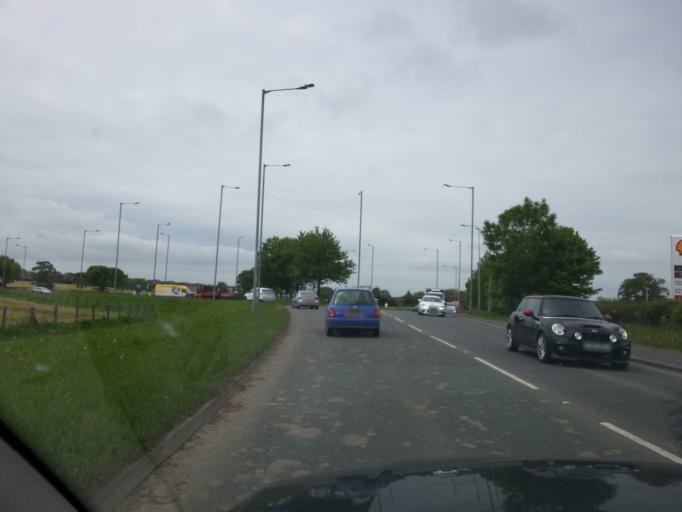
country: GB
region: Wales
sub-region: County of Flintshire
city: Buckley
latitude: 53.1807
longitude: -3.1104
